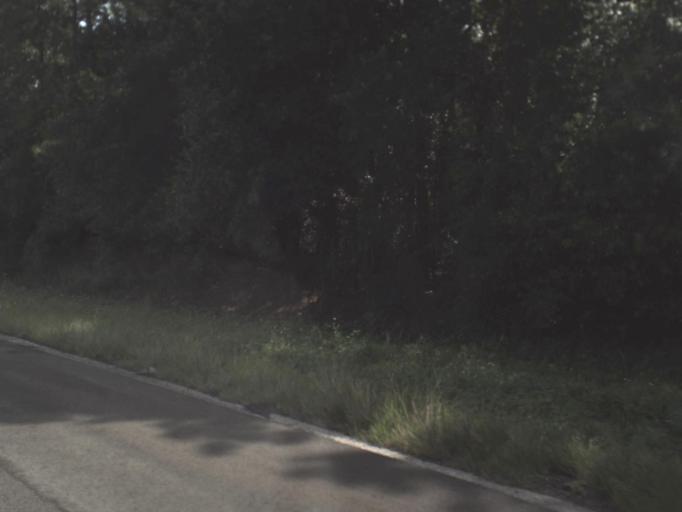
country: US
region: Florida
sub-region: Pasco County
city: San Antonio
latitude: 28.4069
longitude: -82.3029
